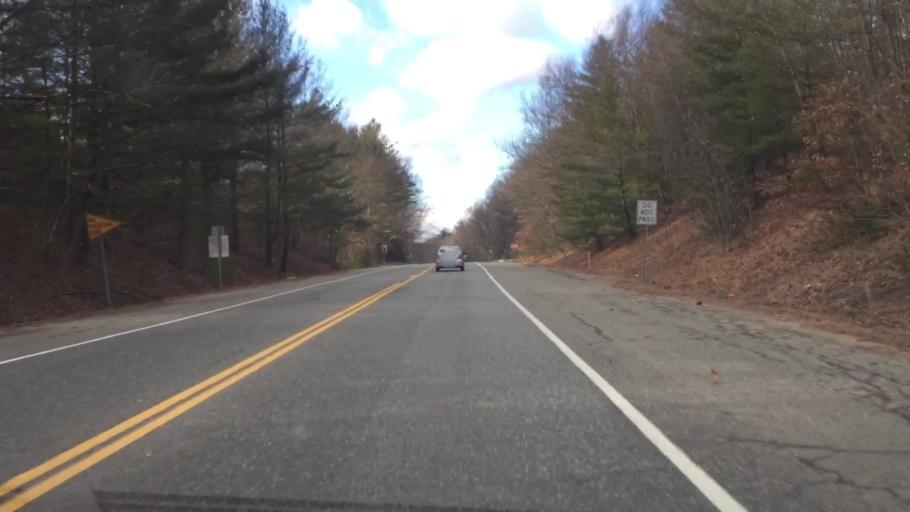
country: US
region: Massachusetts
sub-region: Worcester County
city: West Boylston
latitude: 42.3368
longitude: -71.7476
